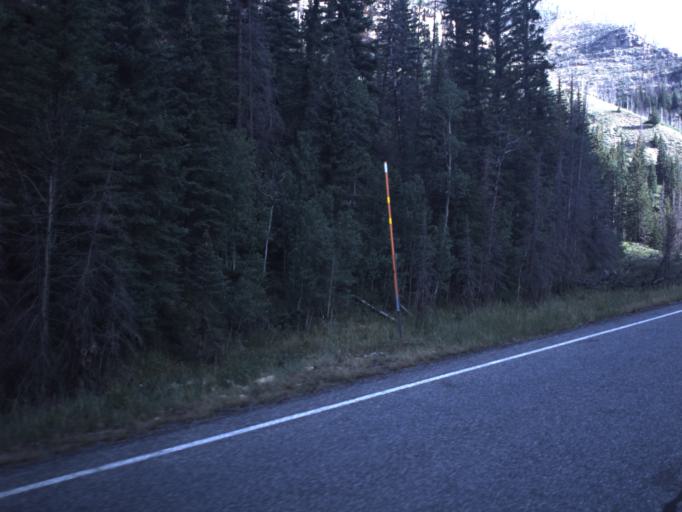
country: US
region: Utah
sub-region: Emery County
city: Huntington
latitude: 39.5135
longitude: -111.1558
